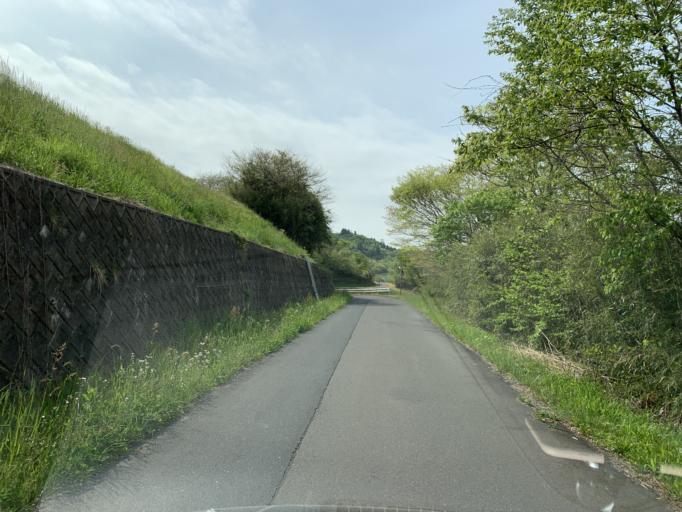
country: JP
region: Iwate
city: Ichinoseki
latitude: 38.9007
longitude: 141.0585
